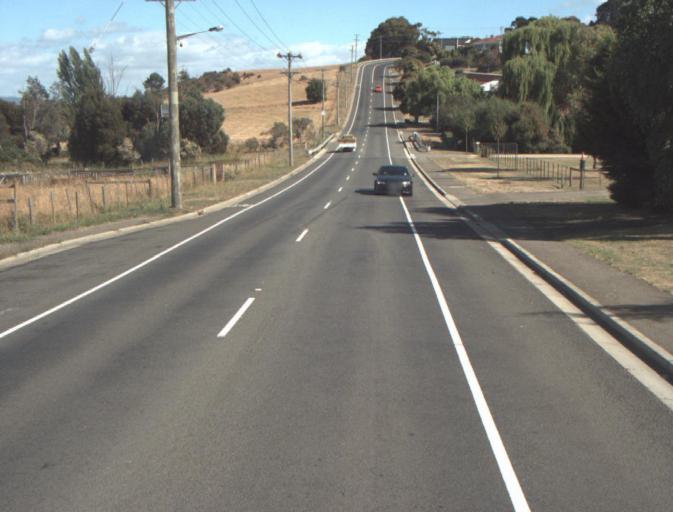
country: AU
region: Tasmania
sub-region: Launceston
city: Newstead
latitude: -41.4336
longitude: 147.1750
